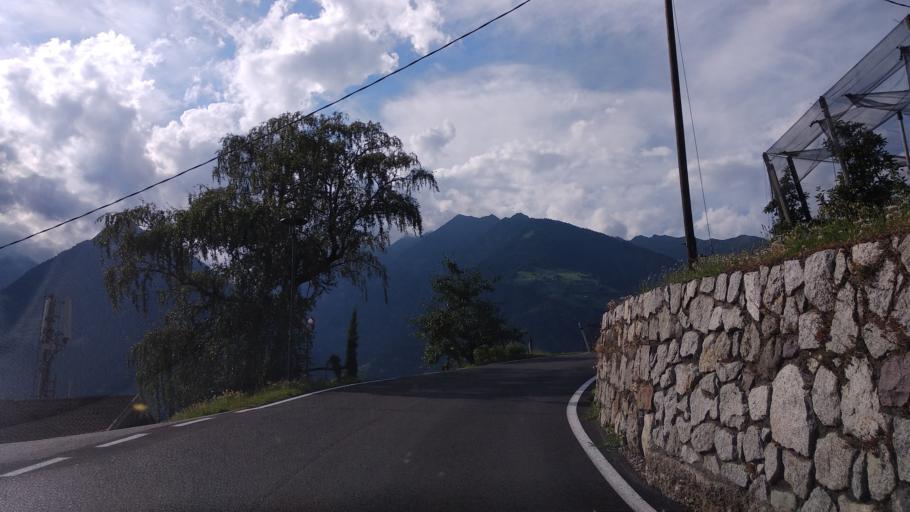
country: IT
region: Trentino-Alto Adige
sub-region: Bolzano
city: Scena
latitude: 46.6891
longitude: 11.1910
